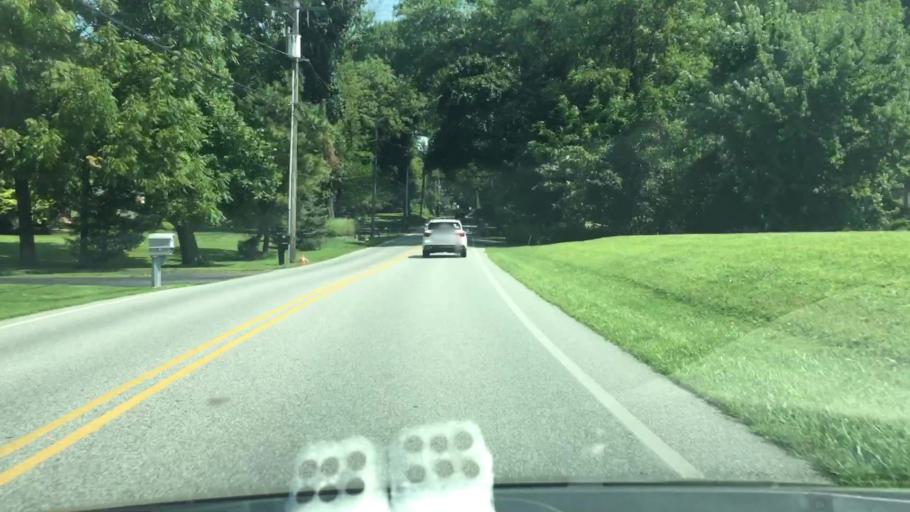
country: US
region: Pennsylvania
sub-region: Delaware County
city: Brookhaven
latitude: 39.8880
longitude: -75.4016
